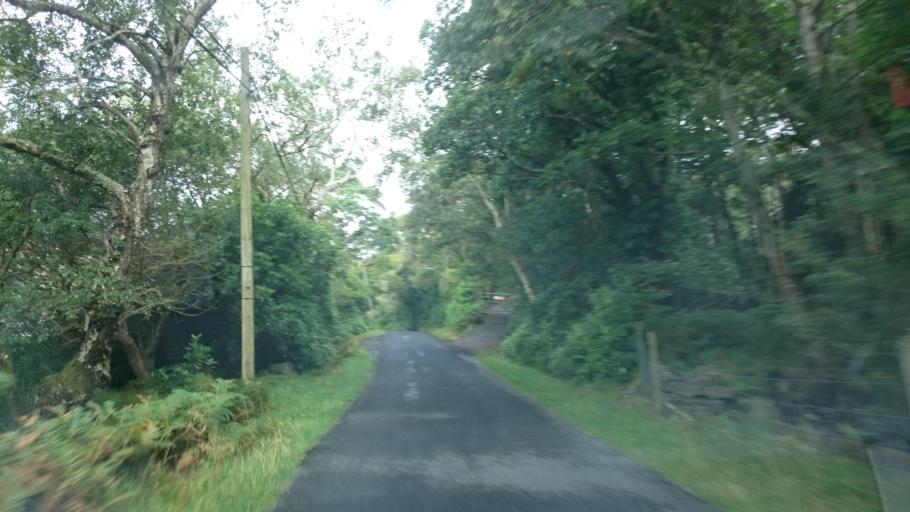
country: IE
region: Connaught
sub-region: Maigh Eo
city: Westport
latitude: 53.9490
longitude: -9.5664
